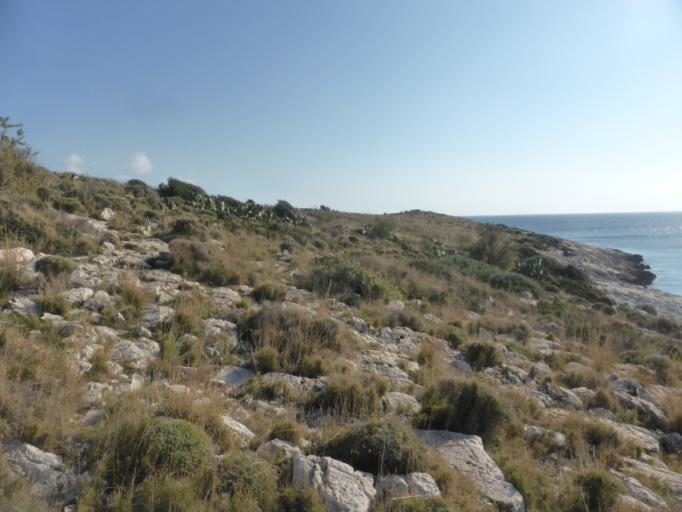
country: GR
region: Attica
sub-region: Nomarchia Anatolikis Attikis
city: Vouliagmeni
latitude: 37.7995
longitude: 23.7862
